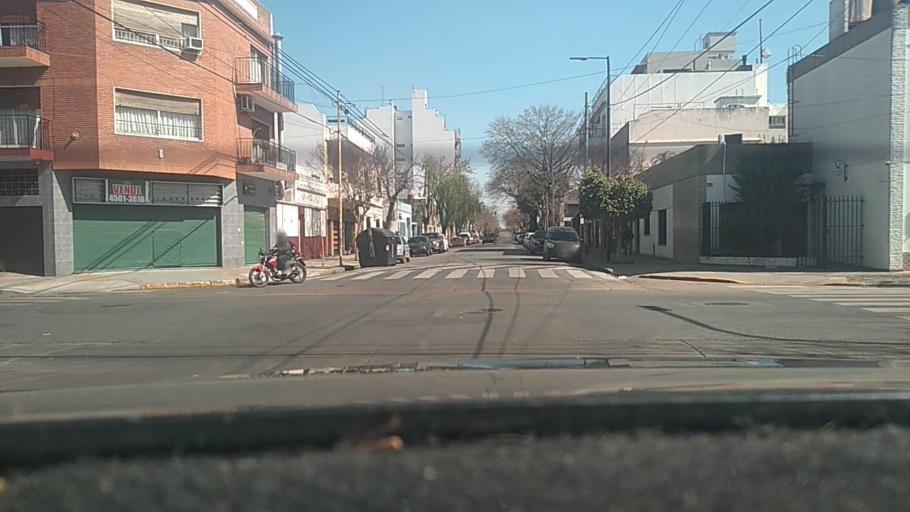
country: AR
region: Buenos Aires F.D.
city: Villa Santa Rita
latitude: -34.6100
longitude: -58.4993
